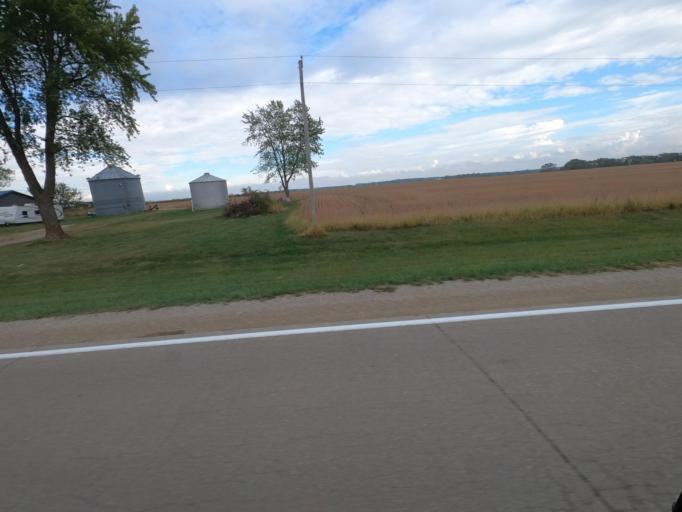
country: US
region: Iowa
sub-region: Henry County
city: Mount Pleasant
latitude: 40.8012
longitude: -91.7042
